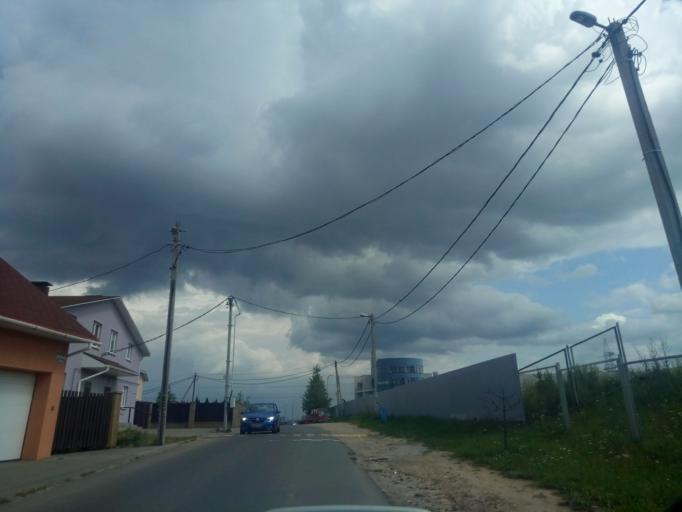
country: BY
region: Minsk
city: Zhdanovichy
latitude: 53.9377
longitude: 27.4215
